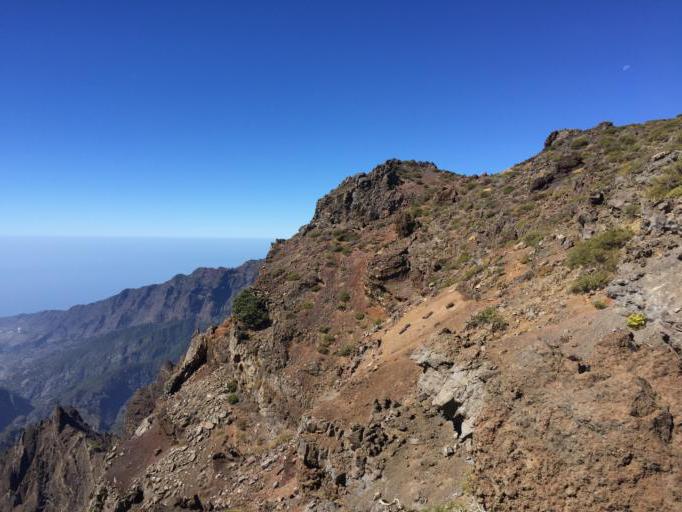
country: ES
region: Canary Islands
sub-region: Provincia de Santa Cruz de Tenerife
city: Garachico
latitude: 28.7426
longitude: -17.8364
